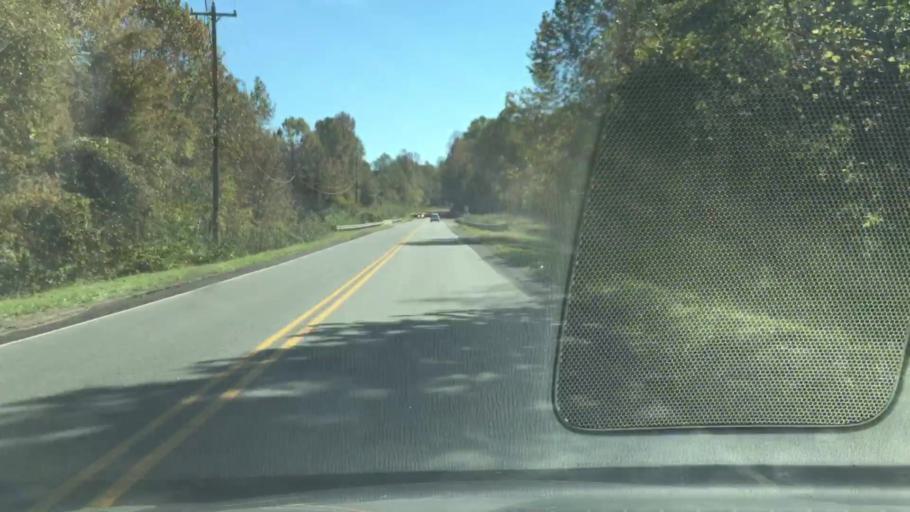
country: US
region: North Carolina
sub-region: Rockingham County
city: Reidsville
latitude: 36.2782
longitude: -79.6502
